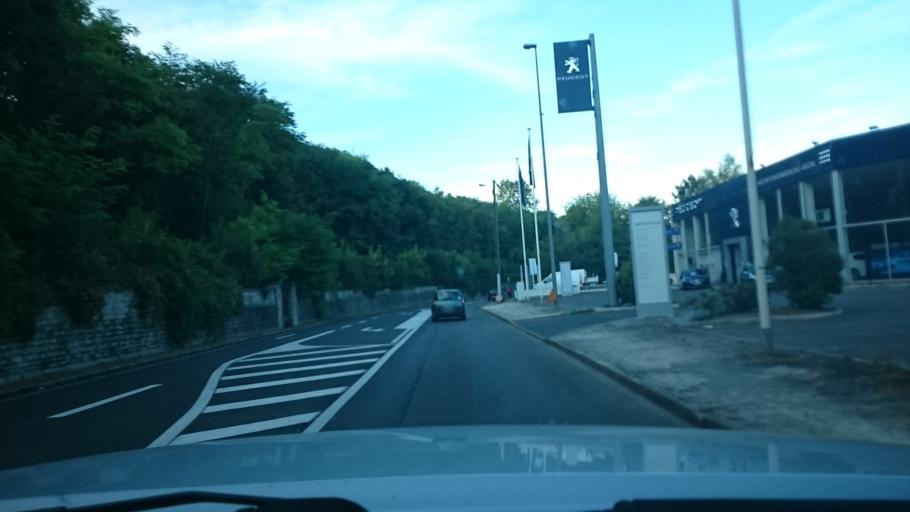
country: FR
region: Ile-de-France
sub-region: Departement de Seine-et-Marne
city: Samoreau
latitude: 48.4244
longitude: 2.7400
